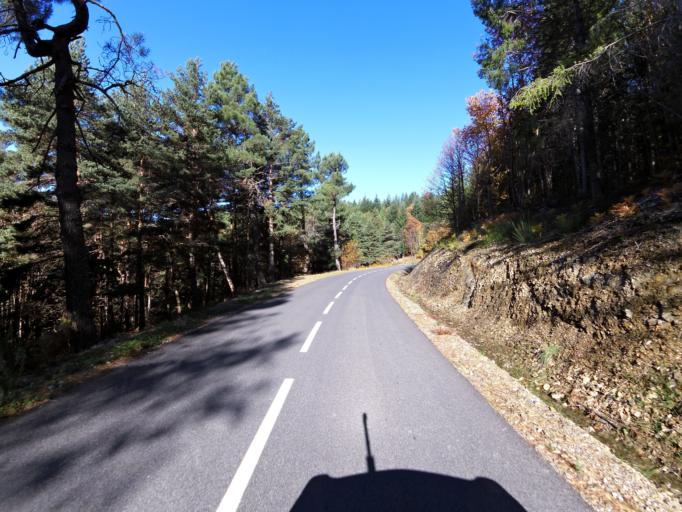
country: FR
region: Rhone-Alpes
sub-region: Departement de l'Ardeche
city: Les Vans
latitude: 44.5029
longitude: 4.1192
